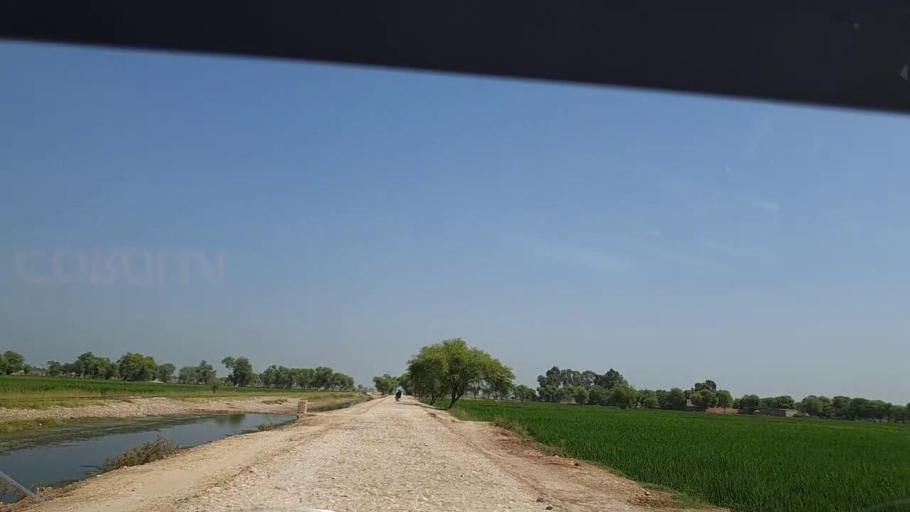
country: PK
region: Sindh
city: Tangwani
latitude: 28.2828
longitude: 69.0300
